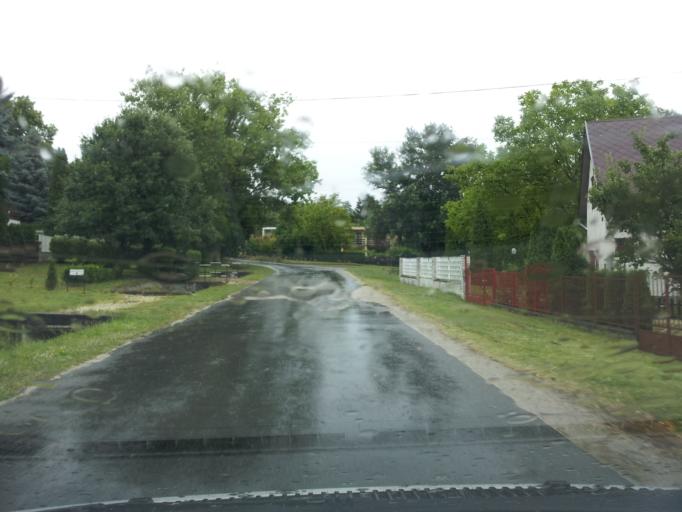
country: HU
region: Veszprem
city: Balatonkenese
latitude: 47.0274
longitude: 18.1313
